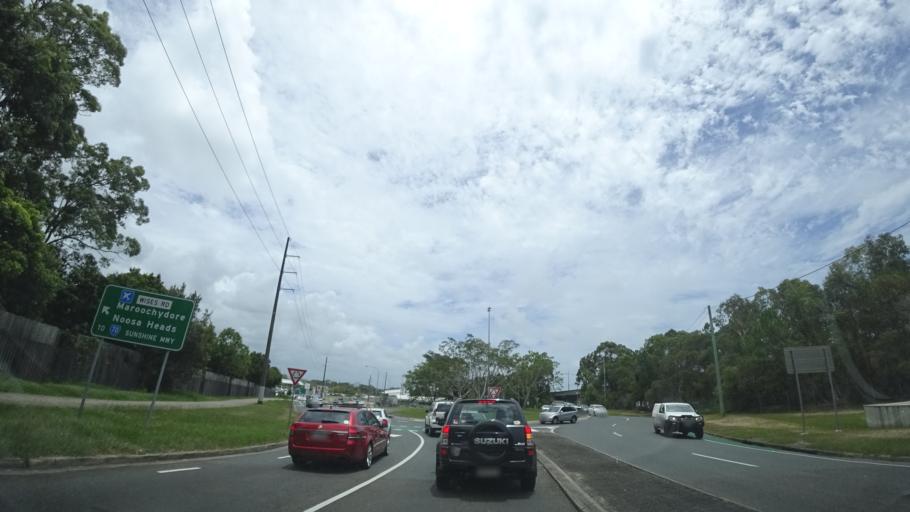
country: AU
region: Queensland
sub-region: Sunshine Coast
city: Mooloolaba
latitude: -26.6742
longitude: 153.0949
